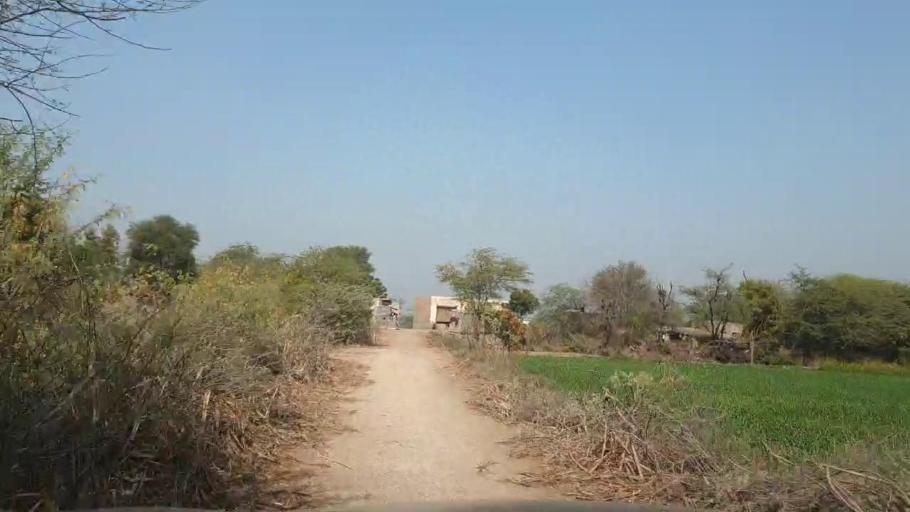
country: PK
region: Sindh
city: Tando Allahyar
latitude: 25.5529
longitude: 68.7243
